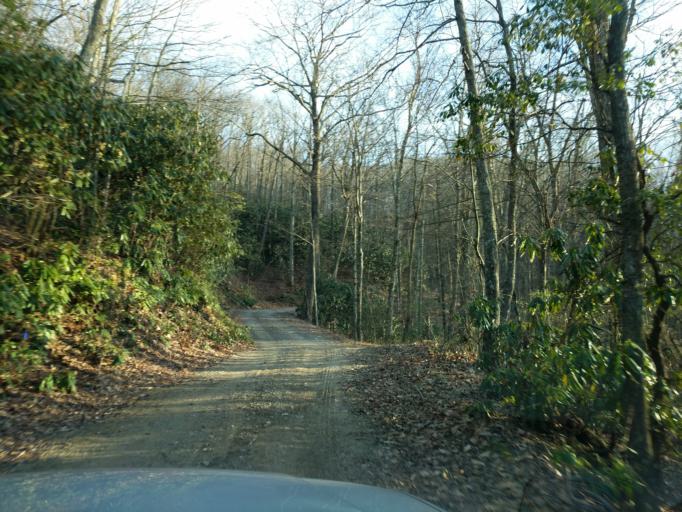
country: US
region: North Carolina
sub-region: Haywood County
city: Cove Creek
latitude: 35.7390
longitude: -83.0555
